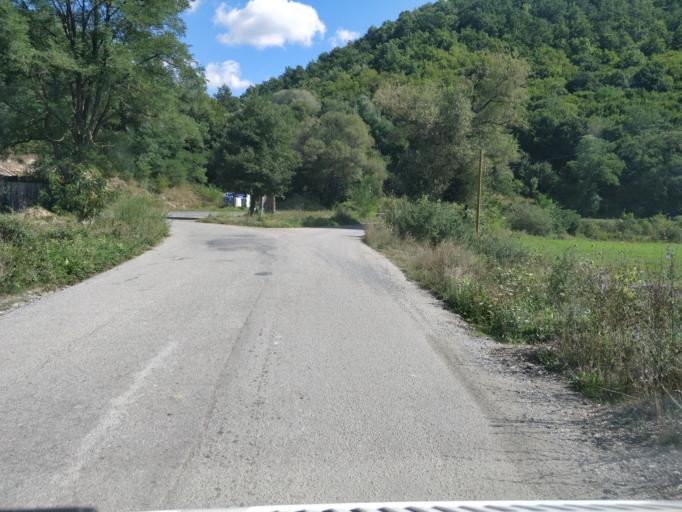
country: RO
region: Cluj
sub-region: Comuna Poeni
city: Poeni
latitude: 46.8933
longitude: 22.8803
